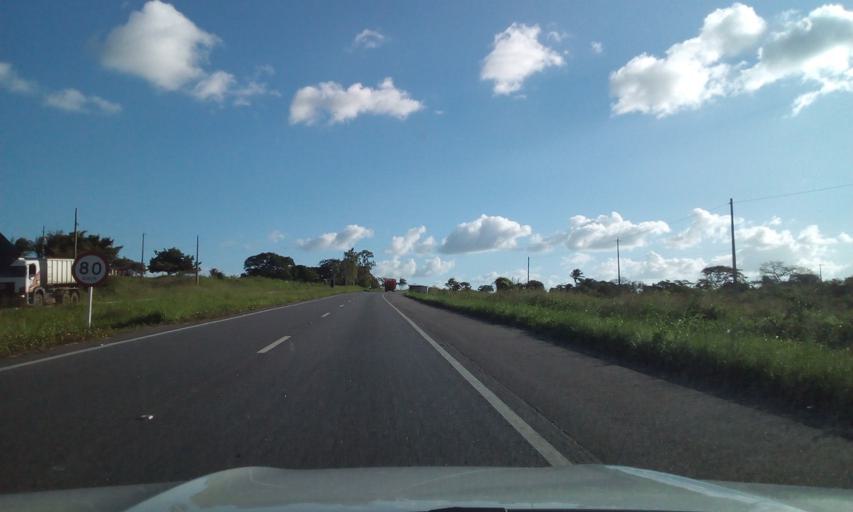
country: BR
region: Paraiba
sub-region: Pilar
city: Pilar
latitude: -7.1854
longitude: -35.1986
